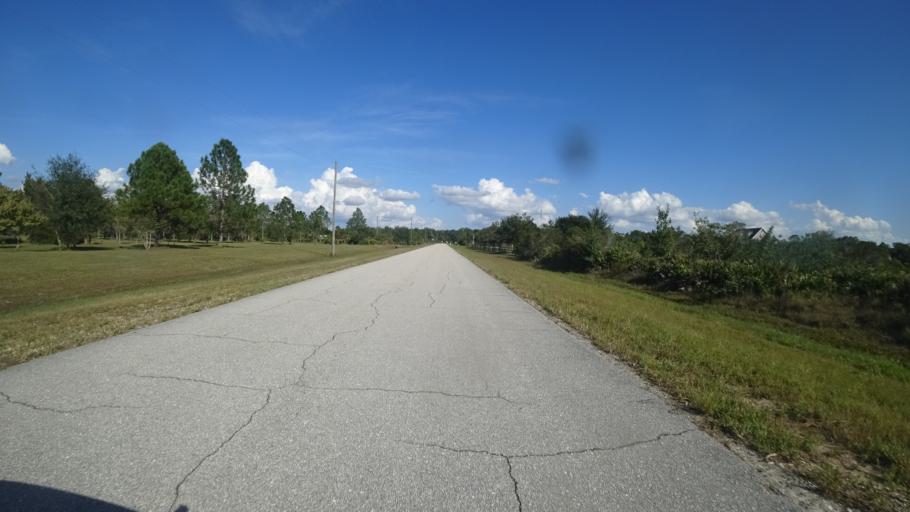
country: US
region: Florida
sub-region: Sarasota County
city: The Meadows
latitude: 27.4159
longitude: -82.2744
